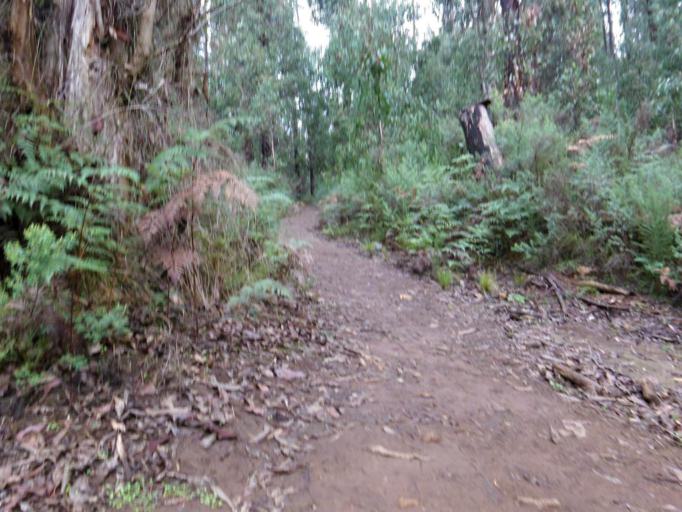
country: AU
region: Victoria
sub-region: Yarra Ranges
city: Millgrove
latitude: -37.5292
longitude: 145.7637
